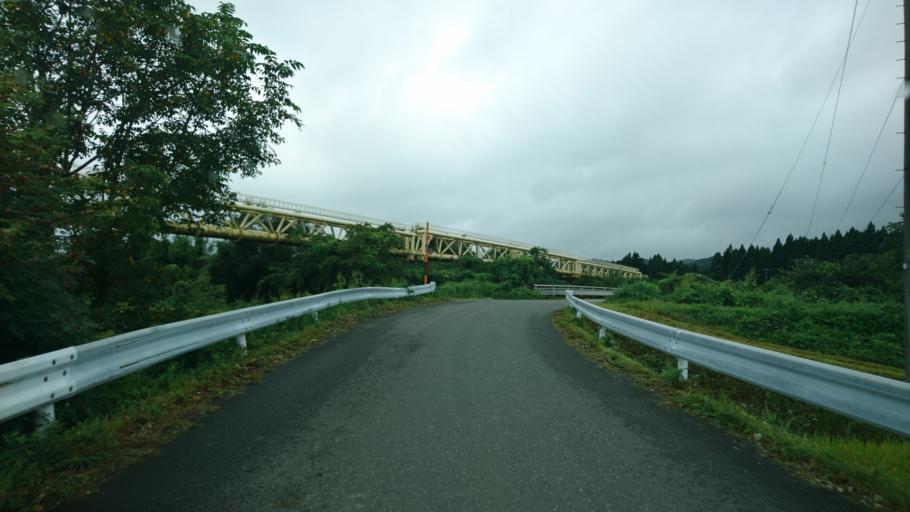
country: JP
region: Iwate
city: Kitakami
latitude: 39.3298
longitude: 140.9817
